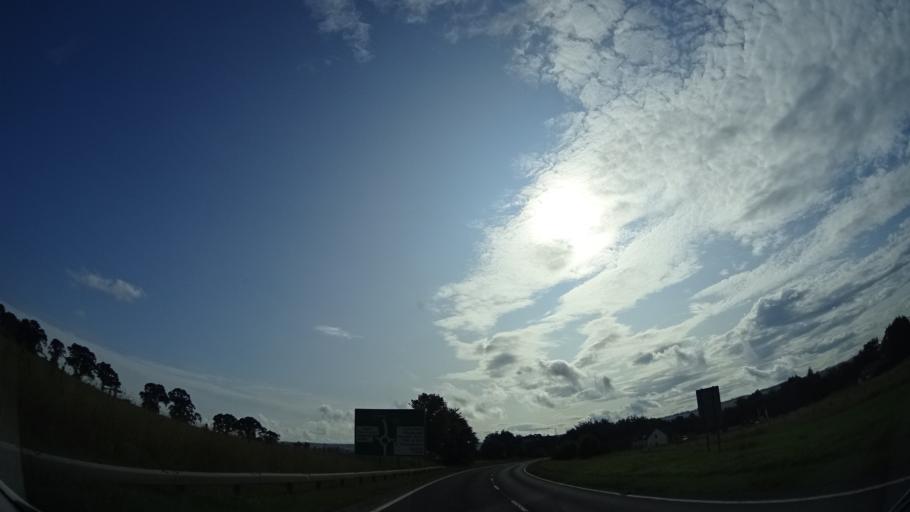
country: GB
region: Scotland
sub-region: Highland
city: Conon Bridge
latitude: 57.5795
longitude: -4.4419
